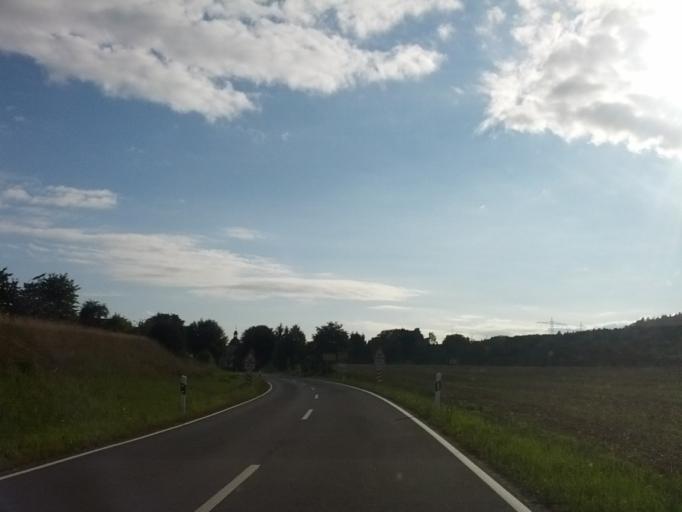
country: DE
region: Thuringia
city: Gerstungen
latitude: 51.0011
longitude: 10.0979
